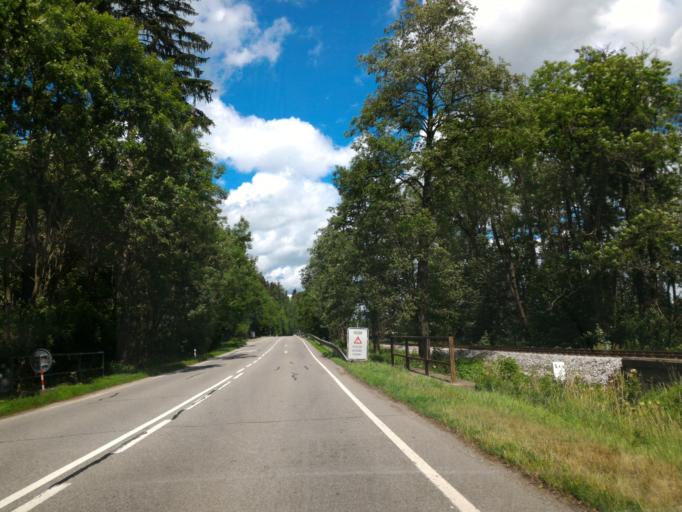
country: CZ
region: Vysocina
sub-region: Okres Jihlava
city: Trest'
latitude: 49.3159
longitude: 15.4807
